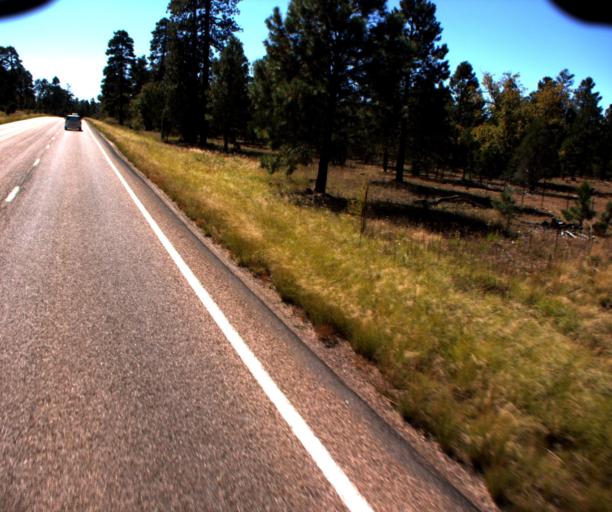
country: US
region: Arizona
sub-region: Navajo County
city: Heber-Overgaard
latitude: 34.3884
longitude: -110.6711
